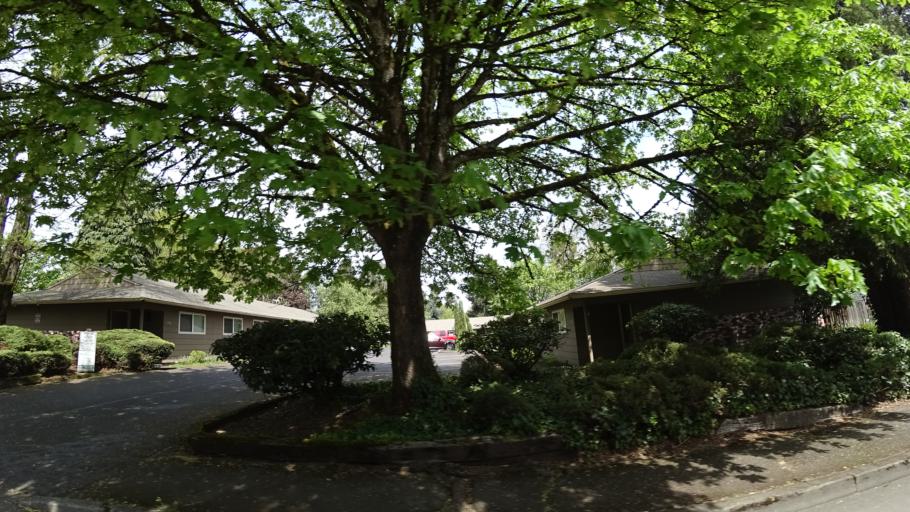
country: US
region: Oregon
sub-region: Clackamas County
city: Oatfield
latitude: 45.4480
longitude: -122.6035
